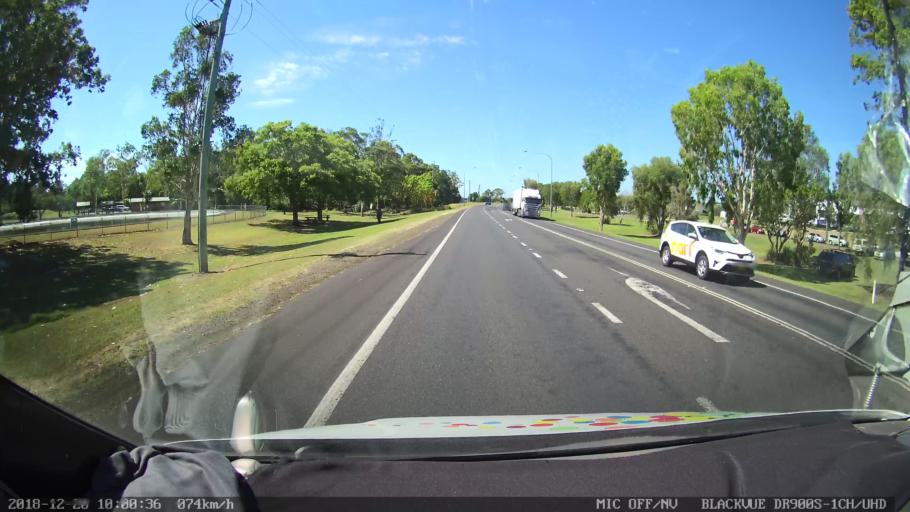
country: AU
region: New South Wales
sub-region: Lismore Municipality
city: Lismore
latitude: -28.8342
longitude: 153.2647
